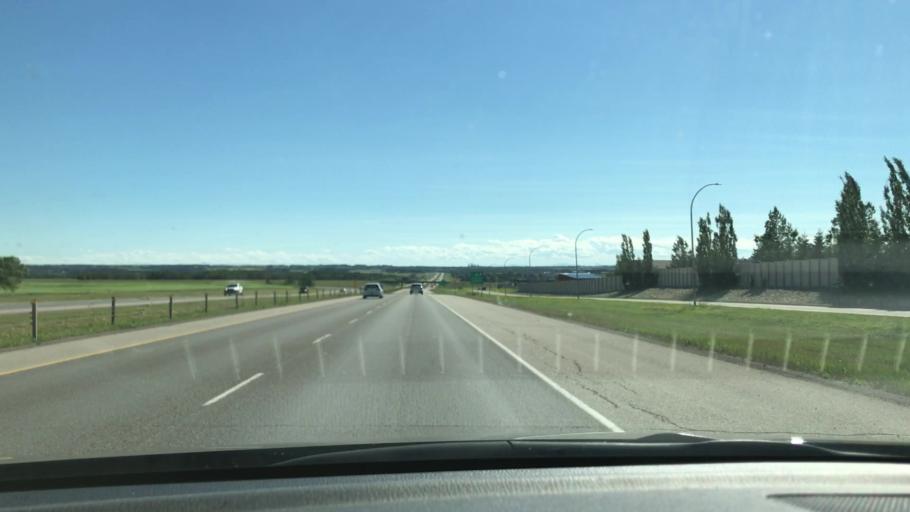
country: CA
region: Alberta
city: Penhold
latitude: 52.0101
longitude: -113.9501
